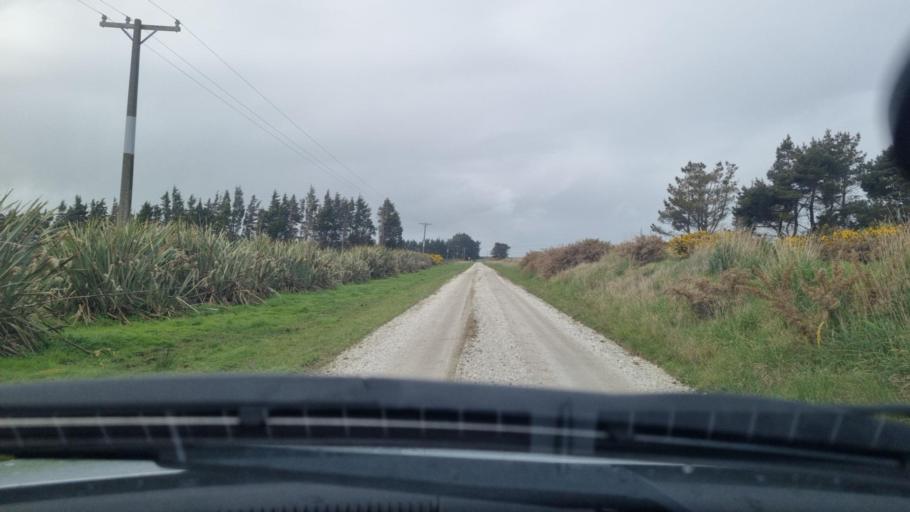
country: NZ
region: Southland
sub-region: Invercargill City
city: Invercargill
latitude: -46.4943
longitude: 168.4232
